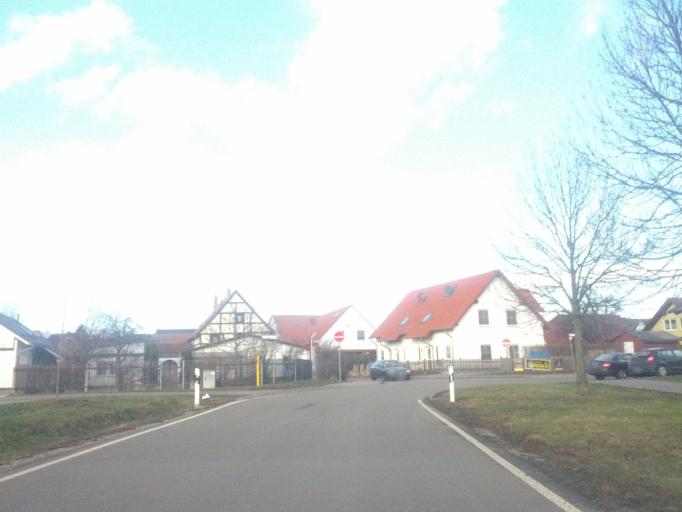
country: DE
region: Thuringia
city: Apfelstadt
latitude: 50.9001
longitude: 10.8905
